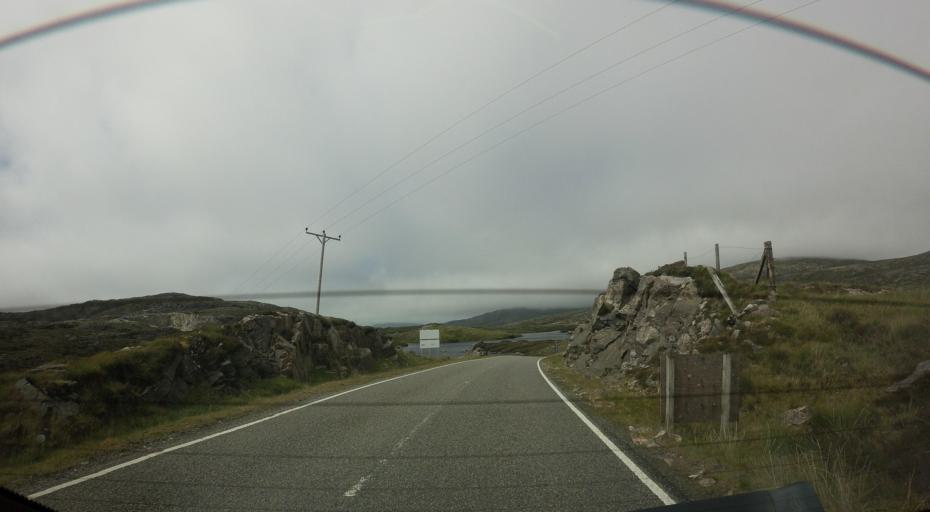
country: GB
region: Scotland
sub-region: Eilean Siar
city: Harris
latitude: 57.8498
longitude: -6.8456
